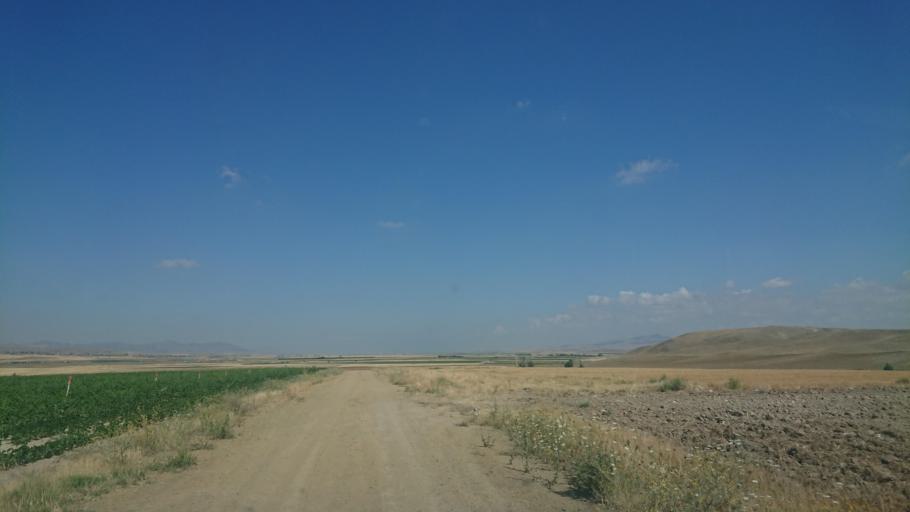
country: TR
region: Aksaray
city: Sariyahsi
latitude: 38.9669
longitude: 33.9227
